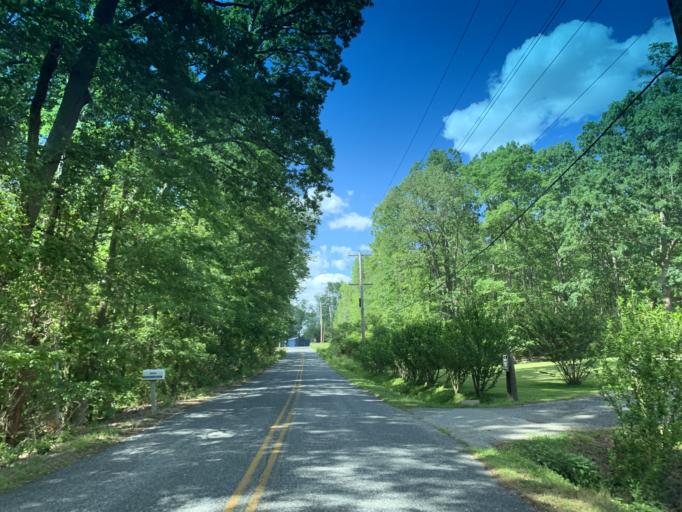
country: US
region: Maryland
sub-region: Cecil County
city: Charlestown
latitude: 39.5475
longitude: -75.9467
